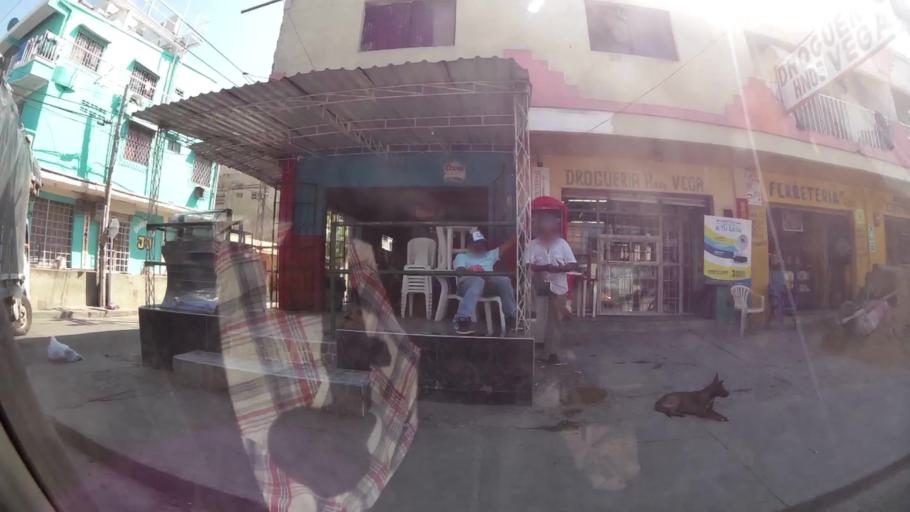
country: CO
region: Bolivar
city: Cartagena
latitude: 10.4097
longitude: -75.5079
